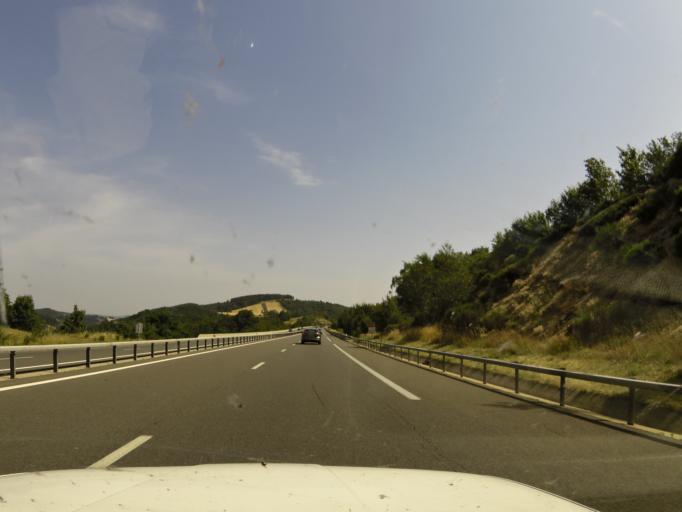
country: FR
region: Languedoc-Roussillon
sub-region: Departement de la Lozere
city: Marvejols
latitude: 44.6178
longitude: 3.2553
